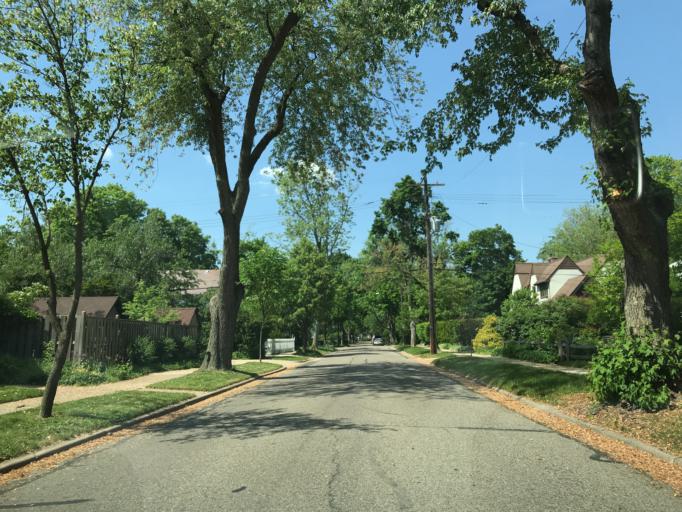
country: US
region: Michigan
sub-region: Washtenaw County
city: Ann Arbor
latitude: 42.2618
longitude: -83.7276
